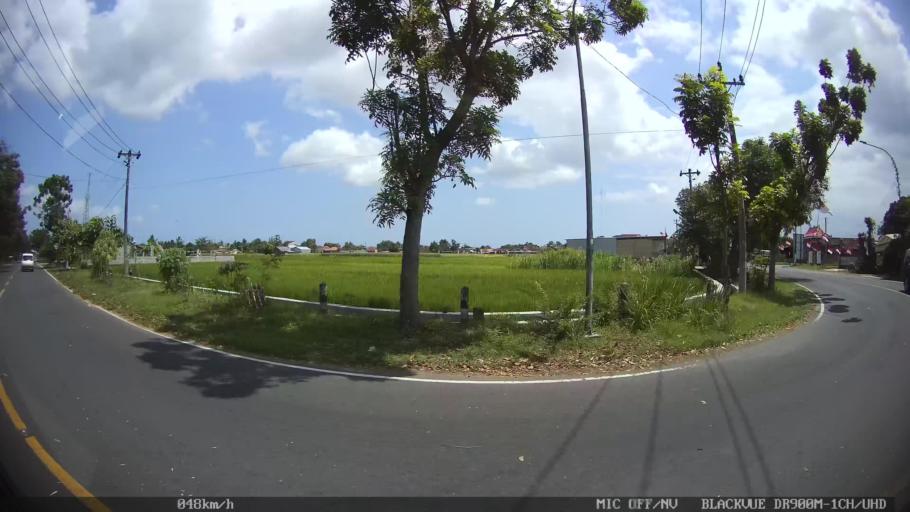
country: ID
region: Daerah Istimewa Yogyakarta
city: Sewon
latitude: -7.8832
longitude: 110.3469
